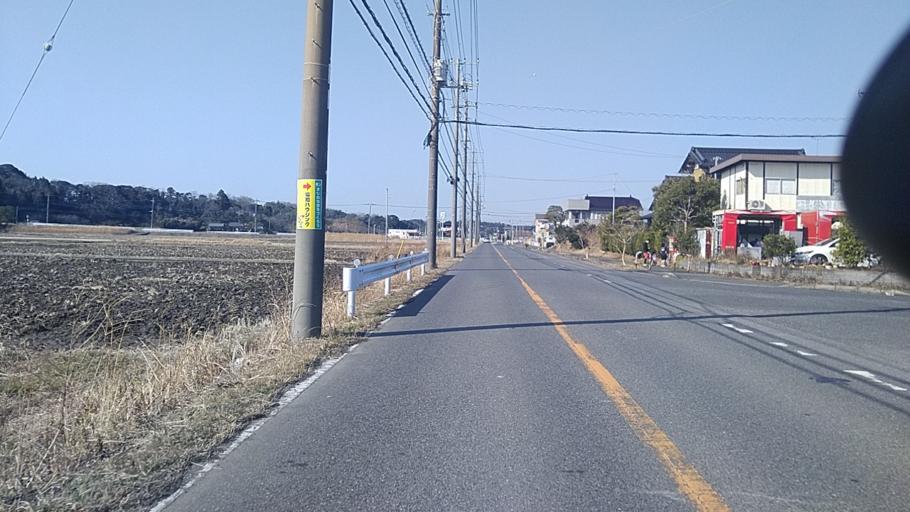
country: JP
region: Chiba
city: Mobara
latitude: 35.4521
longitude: 140.2914
